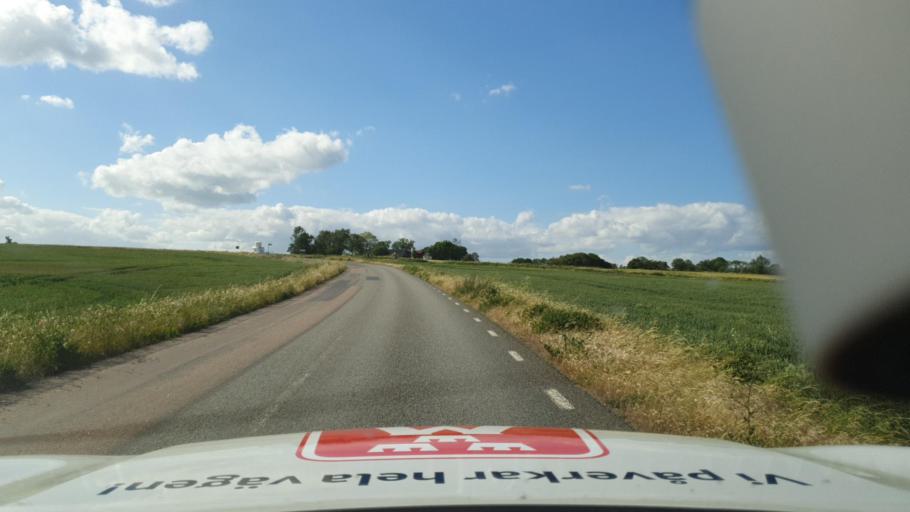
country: SE
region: Skane
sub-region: Simrishamns Kommun
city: Simrishamn
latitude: 55.5628
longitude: 14.3066
